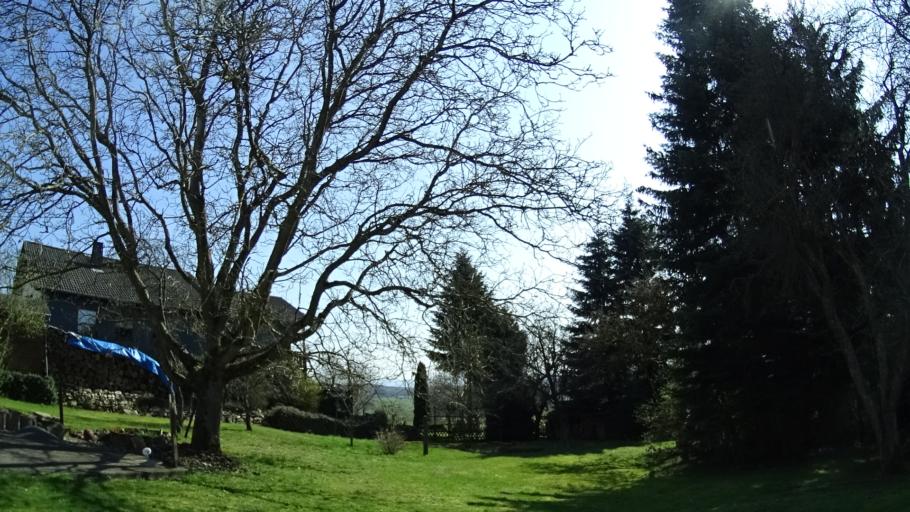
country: DE
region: Rheinland-Pfalz
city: Hattgenstein
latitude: 49.6961
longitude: 7.1586
